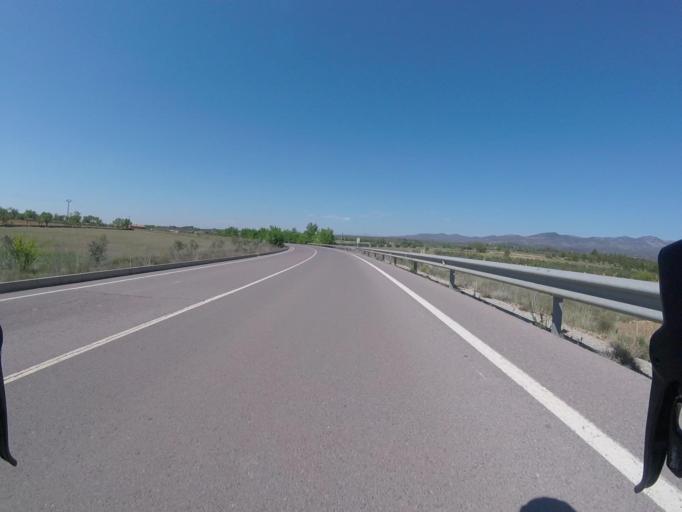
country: ES
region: Valencia
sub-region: Provincia de Castello
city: Benlloch
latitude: 40.2292
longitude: 0.0655
